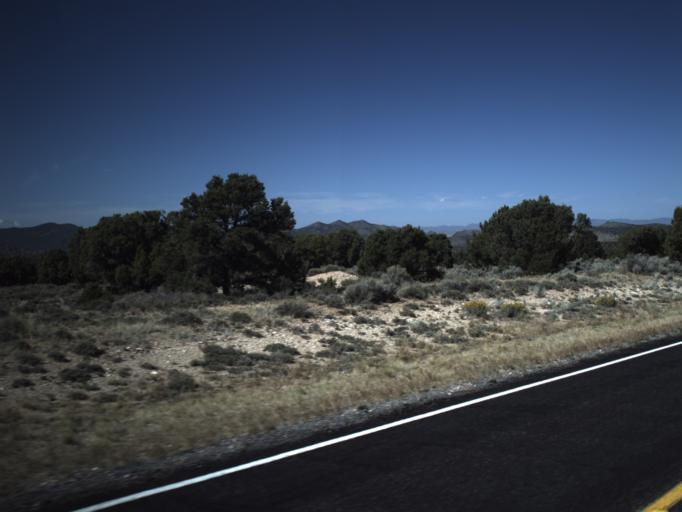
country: US
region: Utah
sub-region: Washington County
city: Enterprise
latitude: 37.6295
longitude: -113.4251
